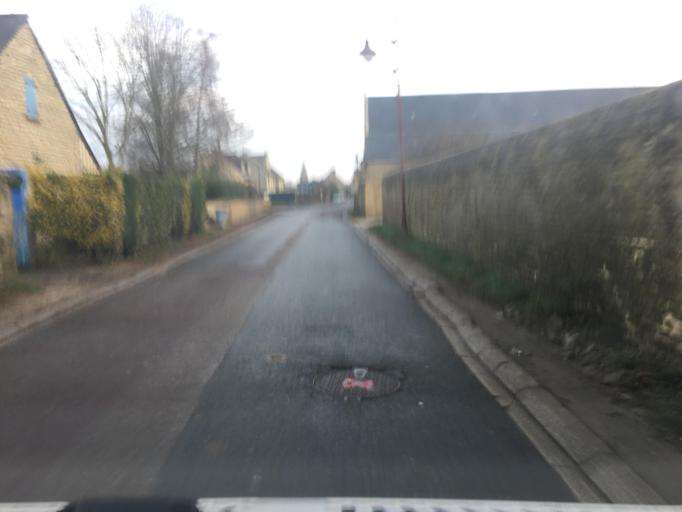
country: FR
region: Lower Normandy
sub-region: Departement du Calvados
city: Creully
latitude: 49.2495
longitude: -0.5647
